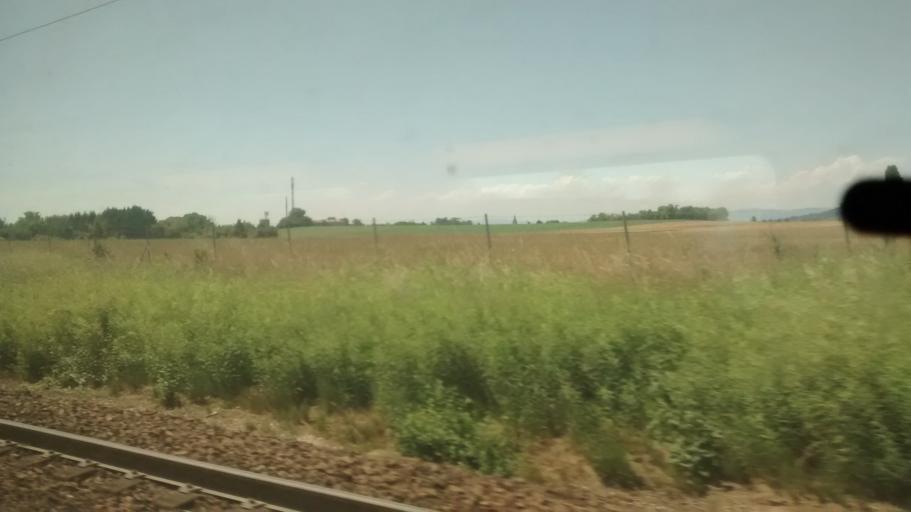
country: FR
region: Rhone-Alpes
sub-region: Departement du Rhone
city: Sathonay-Village
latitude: 45.8400
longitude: 4.8907
